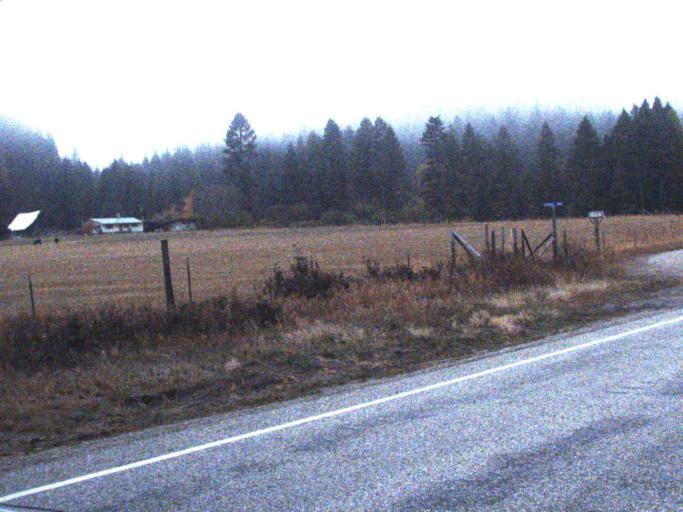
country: US
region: Washington
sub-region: Stevens County
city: Kettle Falls
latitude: 48.7353
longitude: -118.1321
